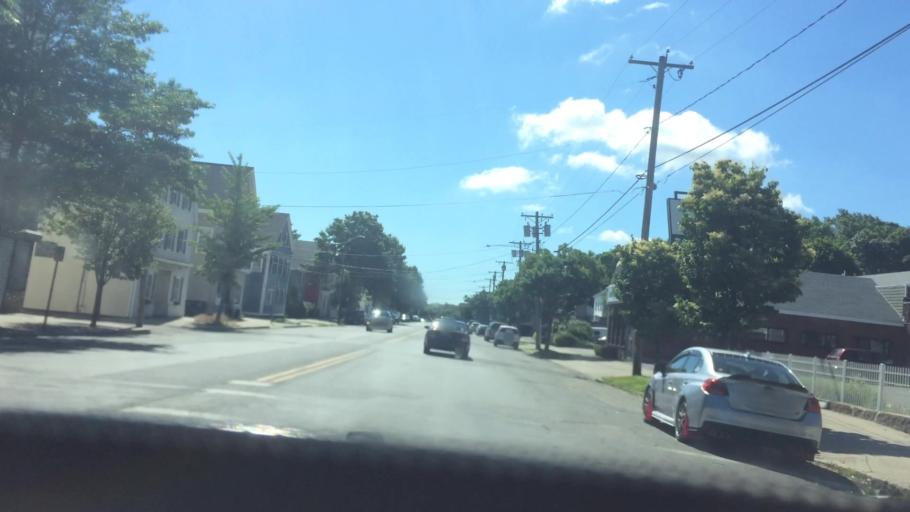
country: US
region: Massachusetts
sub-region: Essex County
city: Peabody
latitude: 42.5219
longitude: -70.9153
